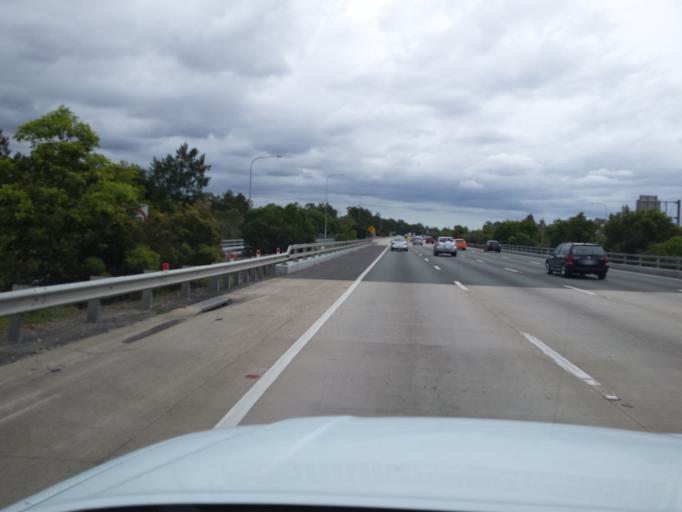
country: AU
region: Queensland
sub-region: Gold Coast
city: Oxenford
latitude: -27.9045
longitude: 153.3162
